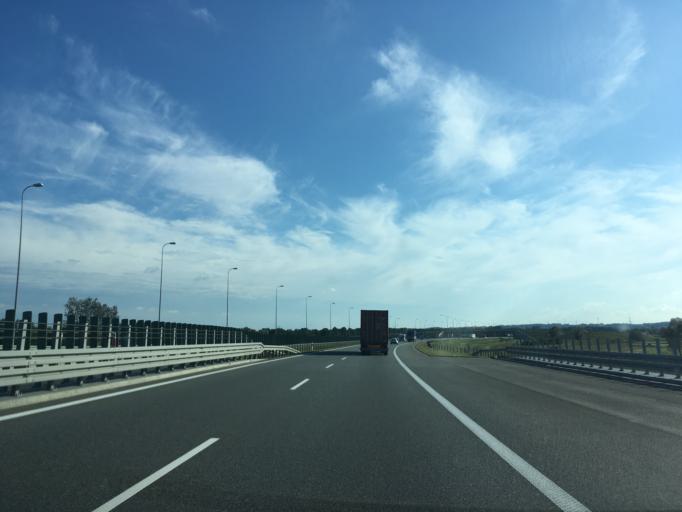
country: PL
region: Kujawsko-Pomorskie
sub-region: Grudziadz
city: Grudziadz
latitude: 53.4329
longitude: 18.6916
